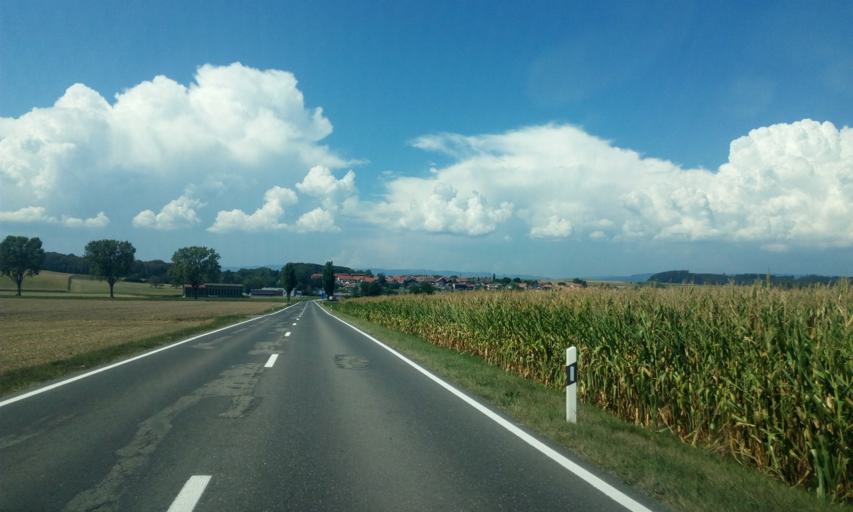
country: CH
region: Fribourg
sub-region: Broye District
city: Domdidier
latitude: 46.8955
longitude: 7.0002
